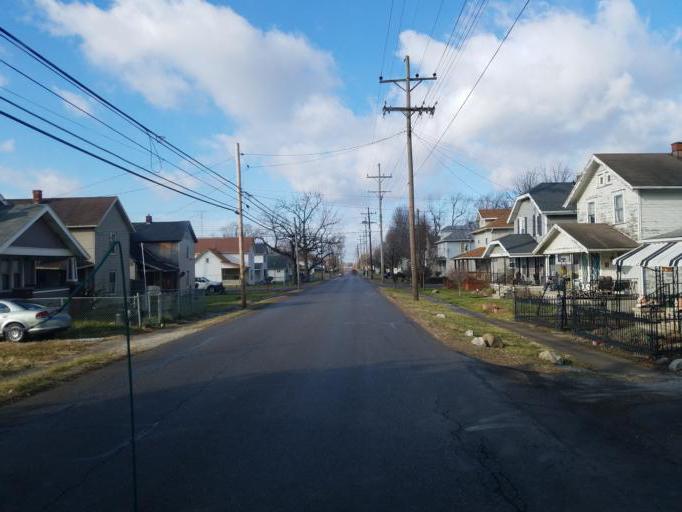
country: US
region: Ohio
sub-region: Marion County
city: Marion
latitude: 40.5859
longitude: -83.1508
